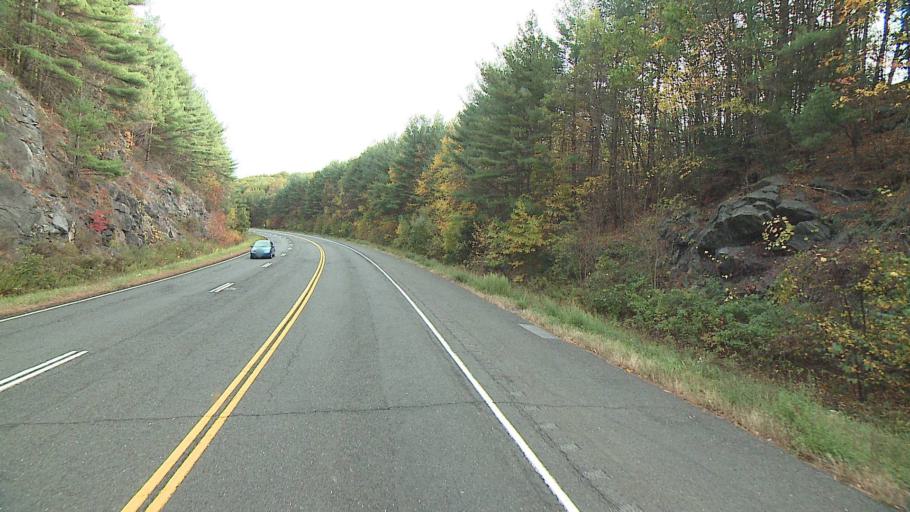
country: US
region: Connecticut
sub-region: Litchfield County
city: Winsted
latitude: 41.9329
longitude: -73.0880
